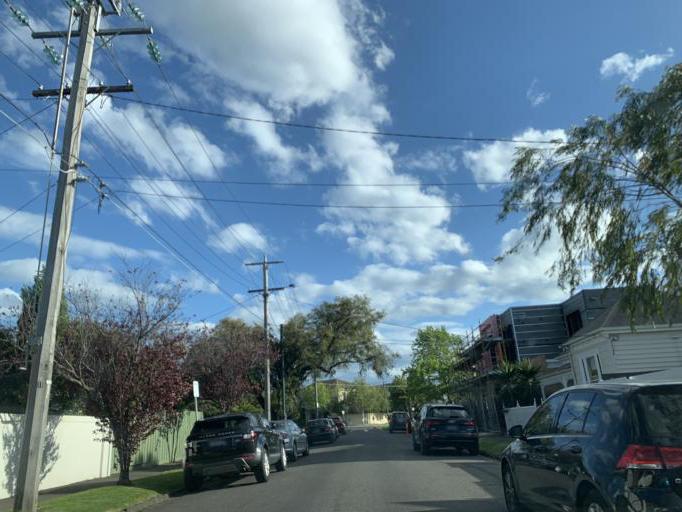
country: AU
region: Victoria
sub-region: Bayside
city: North Brighton
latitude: -37.9056
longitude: 144.9953
